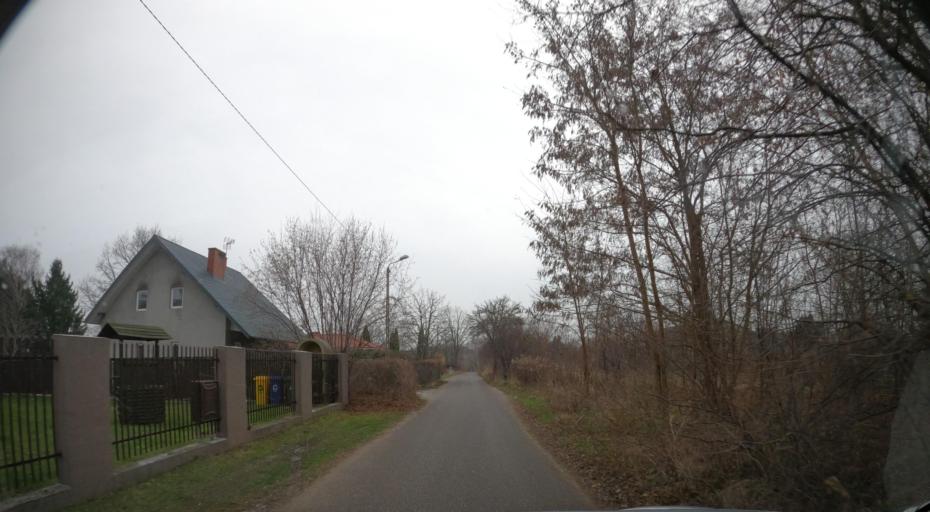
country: PL
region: Masovian Voivodeship
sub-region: Powiat radomski
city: Jastrzebia
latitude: 51.4304
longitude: 21.2305
